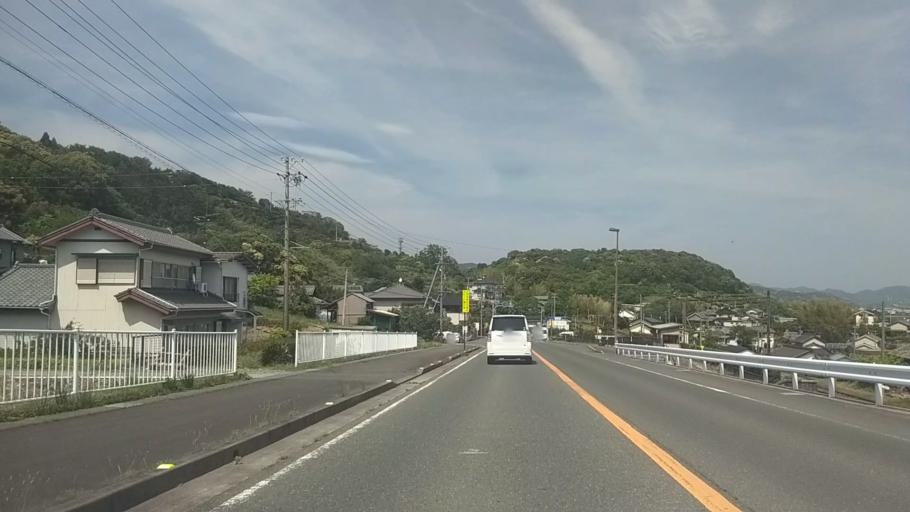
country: JP
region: Shizuoka
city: Kosai-shi
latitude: 34.7895
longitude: 137.6117
